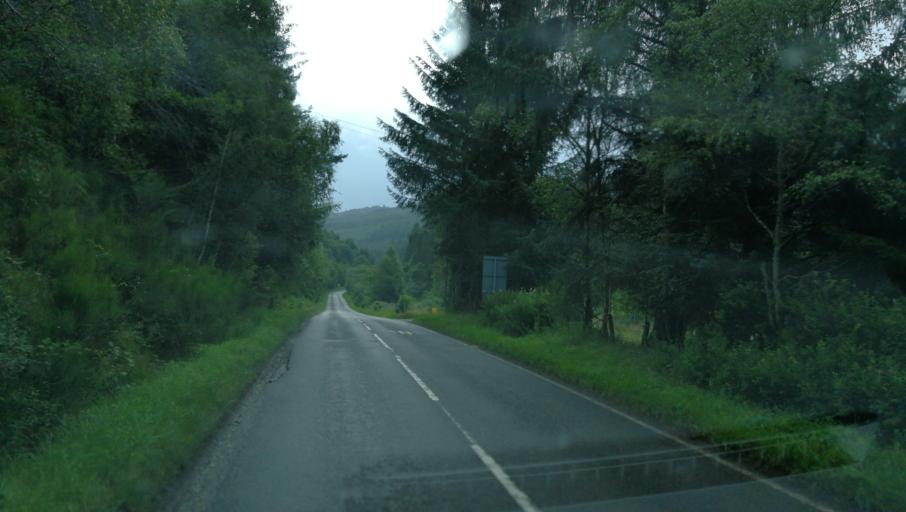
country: GB
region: Scotland
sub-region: Highland
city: Beauly
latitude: 57.3319
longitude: -4.5730
